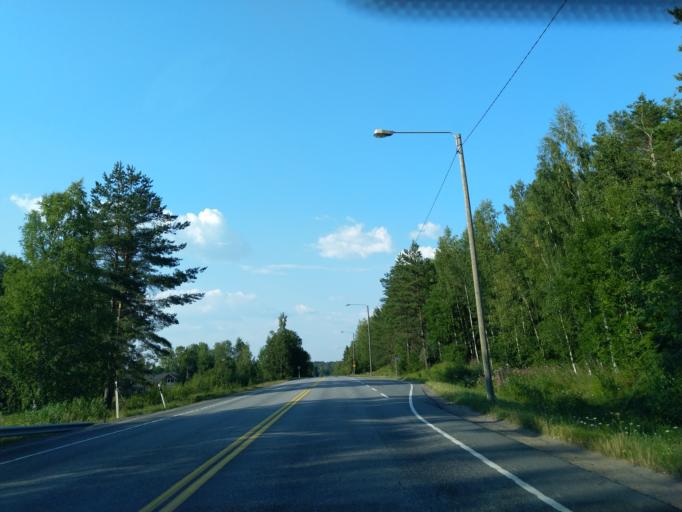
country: FI
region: Satakunta
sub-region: Pori
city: Pomarkku
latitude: 61.6905
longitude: 21.9994
